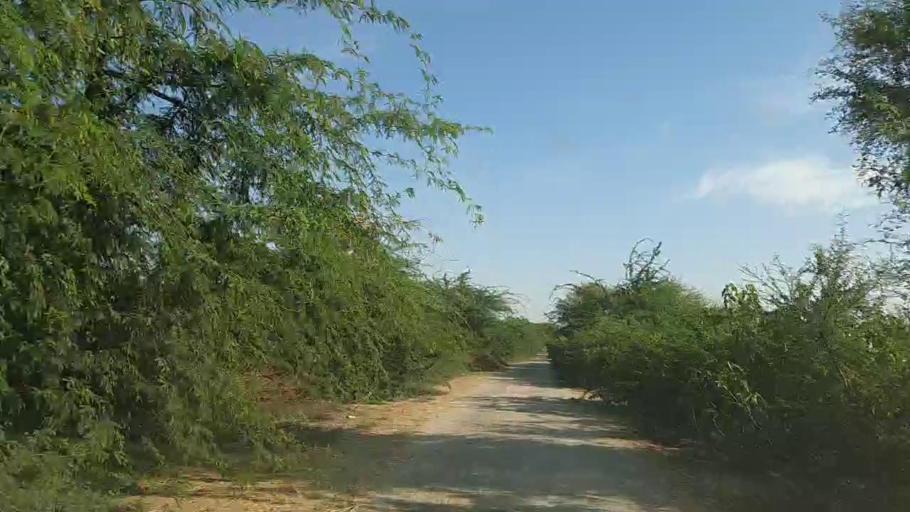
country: PK
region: Sindh
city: Bulri
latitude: 24.7903
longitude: 68.3460
